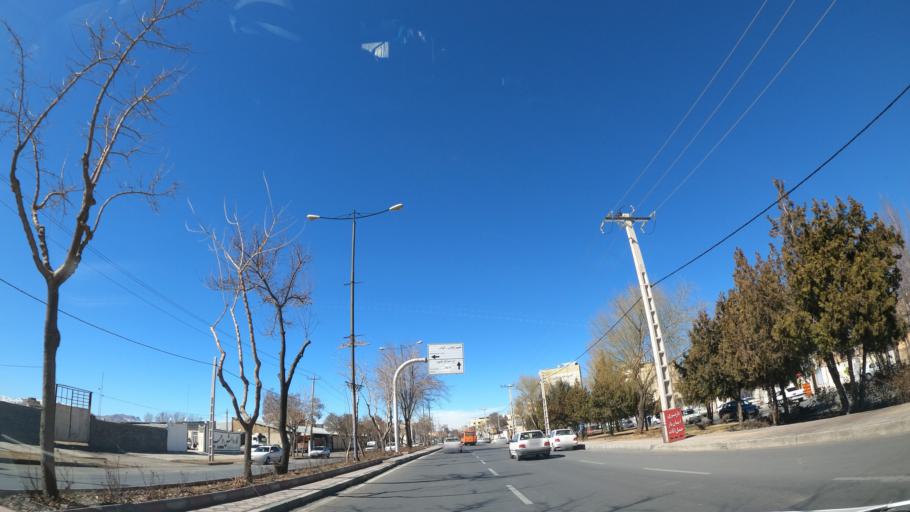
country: IR
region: Chahar Mahall va Bakhtiari
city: Shahrekord
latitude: 32.3139
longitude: 50.8759
